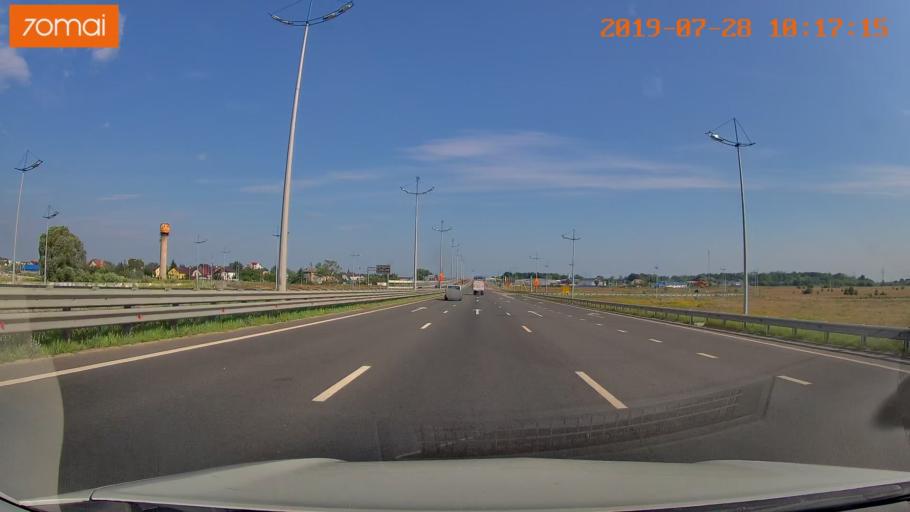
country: RU
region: Kaliningrad
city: Maloye Isakovo
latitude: 54.7375
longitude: 20.5955
